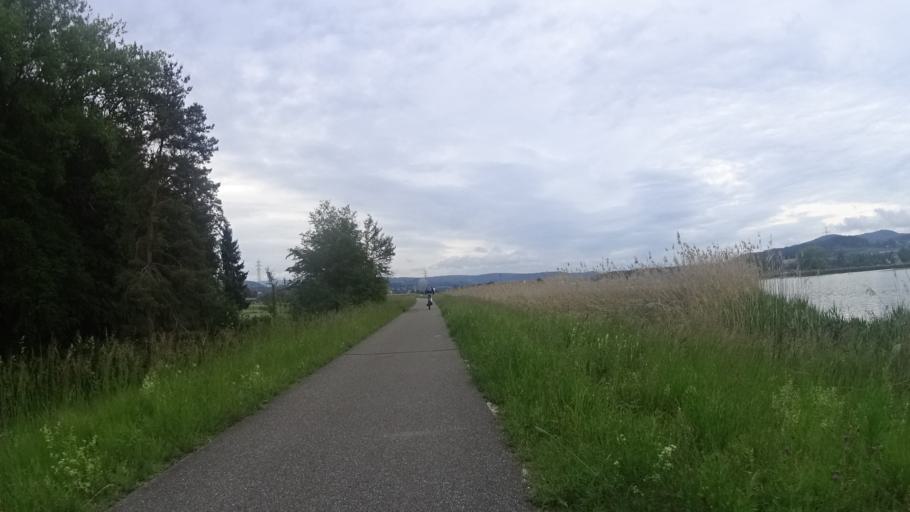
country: CH
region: Aargau
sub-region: Bezirk Zurzach
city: Koblenz
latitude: 47.5904
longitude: 8.2315
